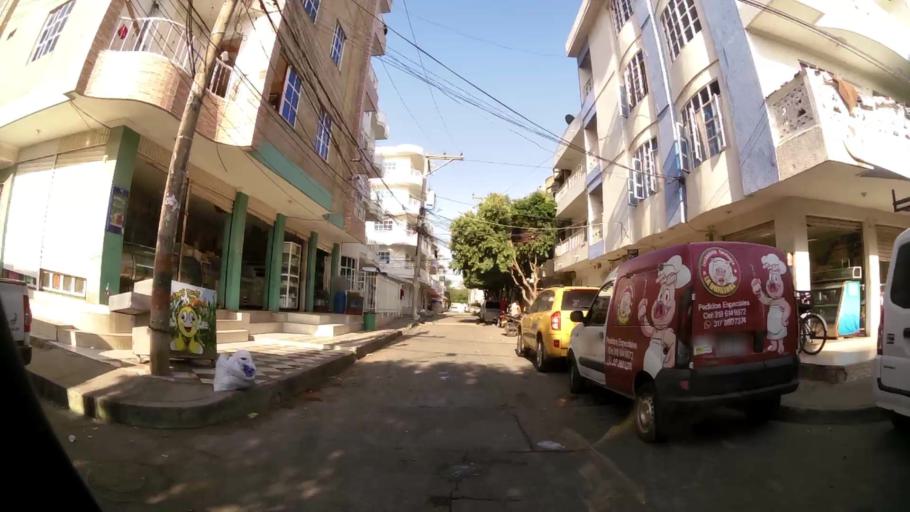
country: CO
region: Bolivar
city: Cartagena
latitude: 10.4004
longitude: -75.4852
